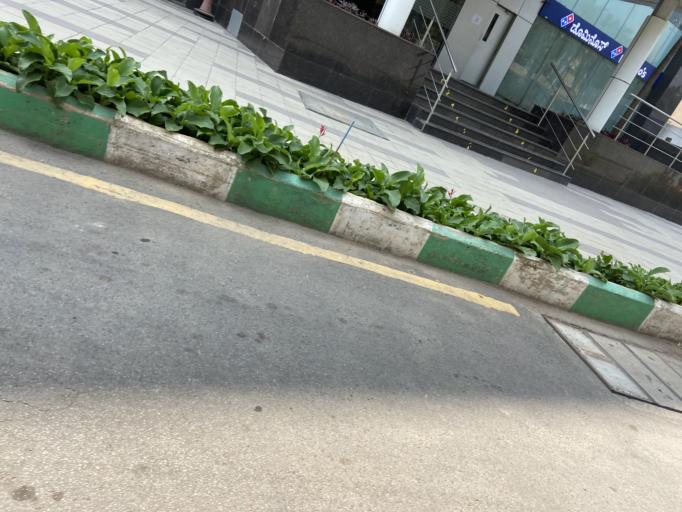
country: IN
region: Karnataka
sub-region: Bangalore Urban
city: Bangalore
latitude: 12.9797
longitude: 77.6581
